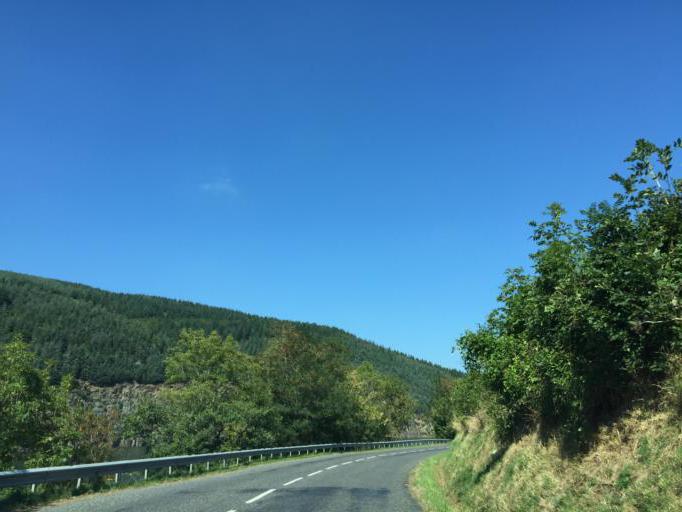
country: FR
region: Rhone-Alpes
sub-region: Departement de la Loire
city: Saint-Paul-en-Jarez
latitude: 45.4372
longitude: 4.5740
